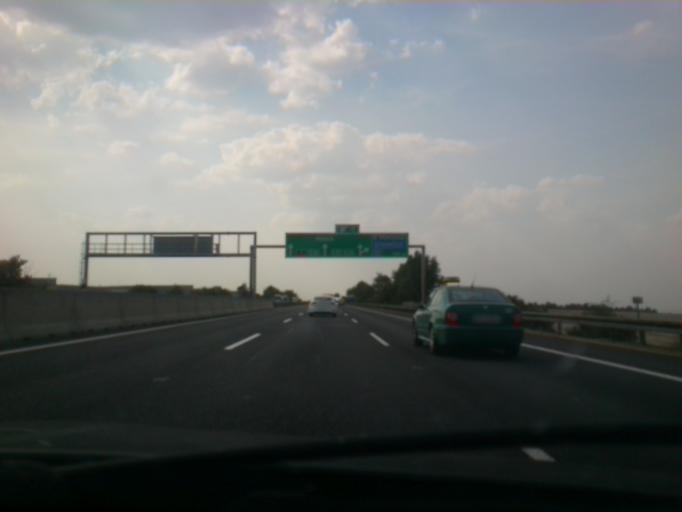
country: CZ
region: Central Bohemia
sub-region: Okres Praha-Vychod
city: Strancice
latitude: 49.9420
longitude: 14.6661
